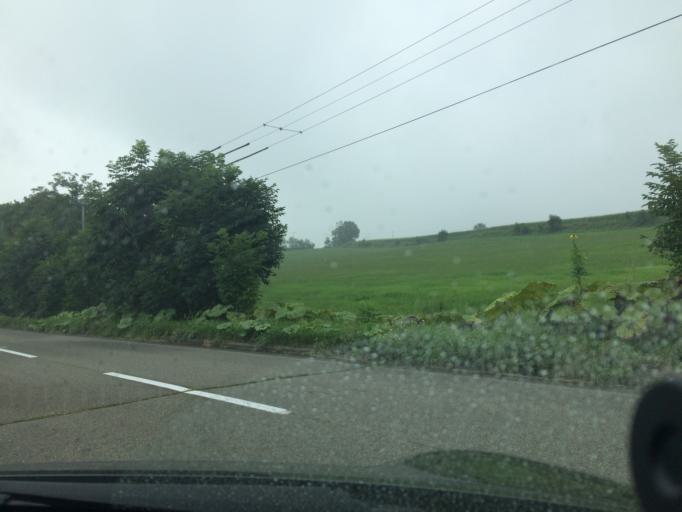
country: JP
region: Hokkaido
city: Otofuke
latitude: 43.0160
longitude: 143.0763
